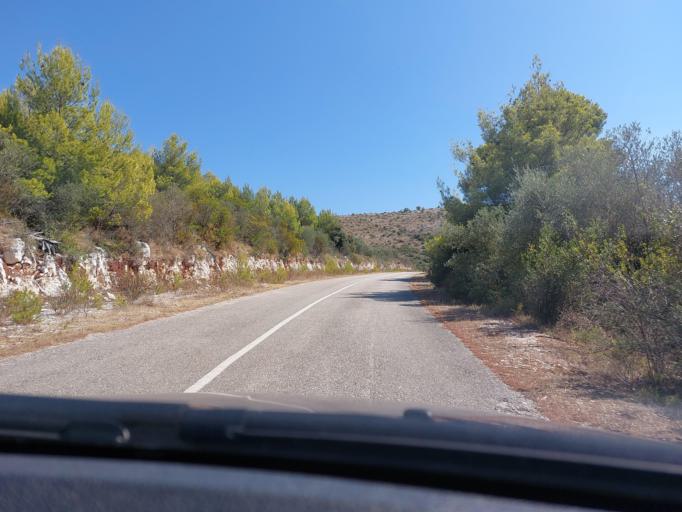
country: HR
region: Dubrovacko-Neretvanska
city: Smokvica
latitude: 42.7516
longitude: 16.8780
